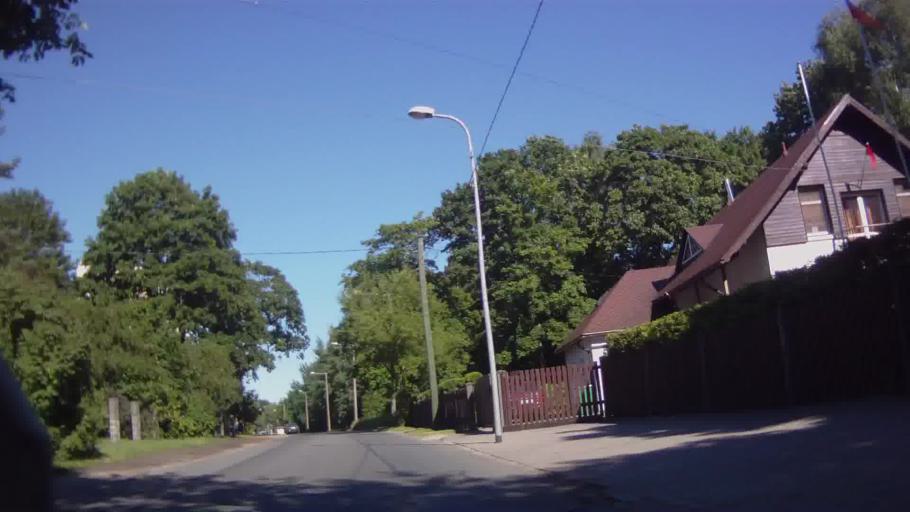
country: LV
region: Riga
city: Riga
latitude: 56.9127
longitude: 24.1178
